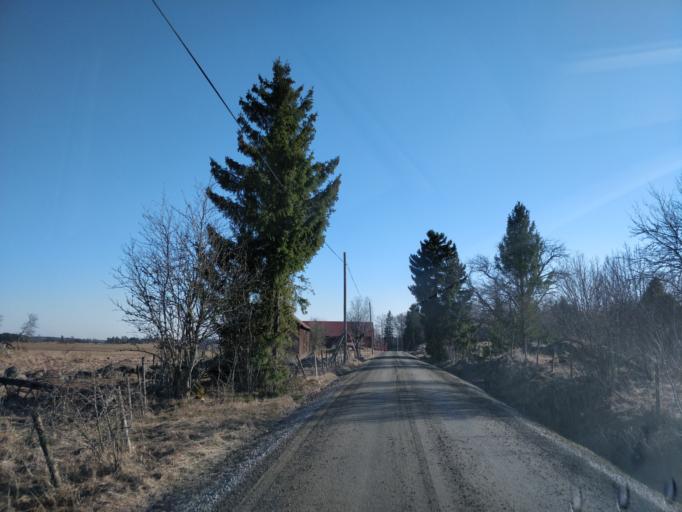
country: SE
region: Uppsala
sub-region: Enkopings Kommun
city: Enkoping
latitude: 59.8232
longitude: 17.1222
